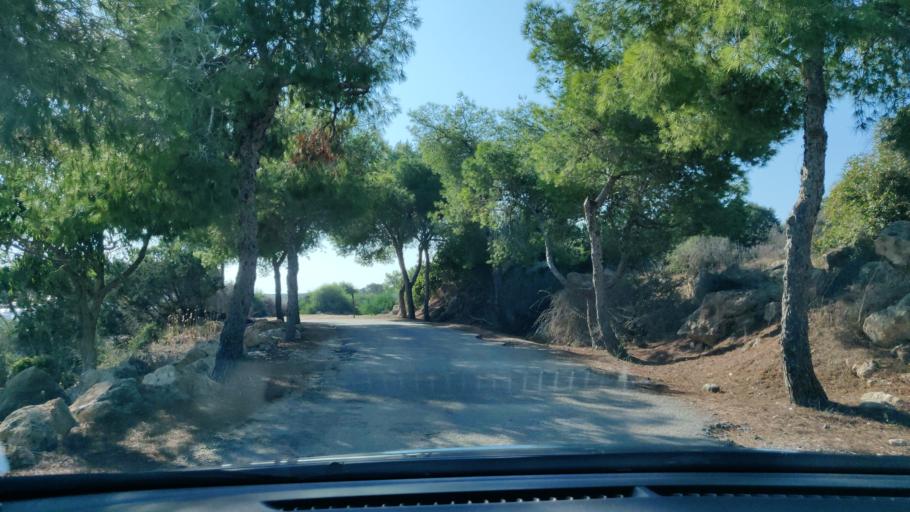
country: CY
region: Ammochostos
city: Protaras
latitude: 34.9819
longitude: 34.0680
